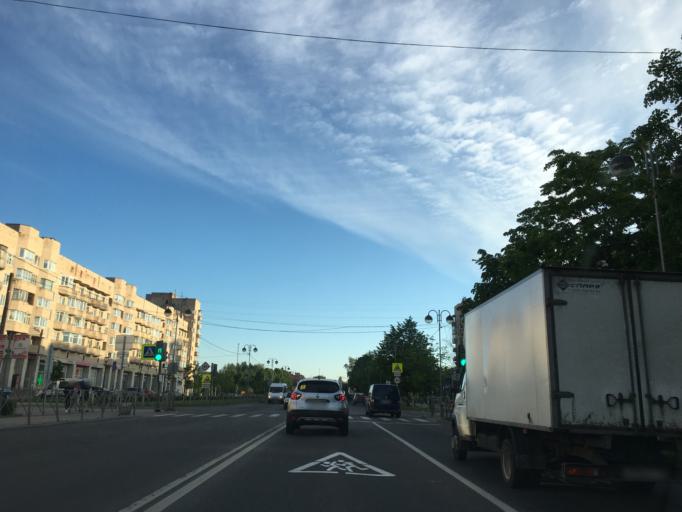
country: RU
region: Leningrad
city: Gatchina
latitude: 59.5787
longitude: 30.1361
